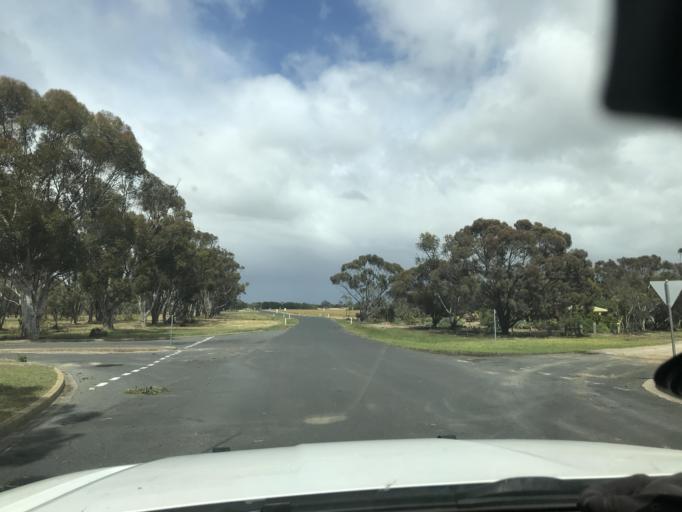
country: AU
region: South Australia
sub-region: Tatiara
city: Bordertown
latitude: -36.3794
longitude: 141.2355
